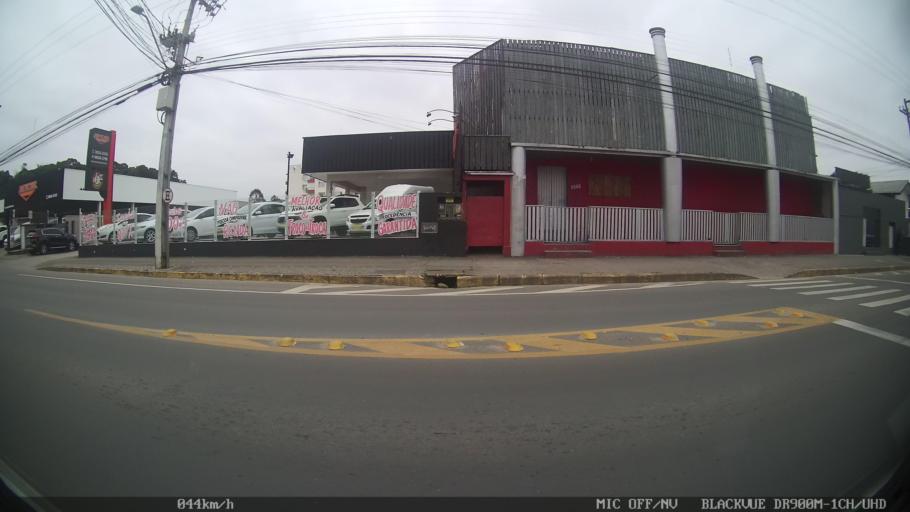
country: BR
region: Santa Catarina
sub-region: Joinville
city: Joinville
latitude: -26.3449
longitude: -48.8472
